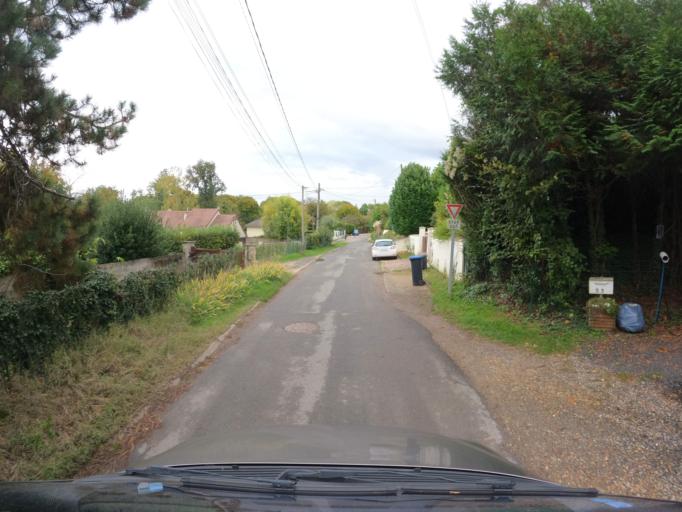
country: FR
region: Ile-de-France
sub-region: Departement de Seine-et-Marne
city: Saint-Germain-sur-Morin
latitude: 48.8742
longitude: 2.8412
